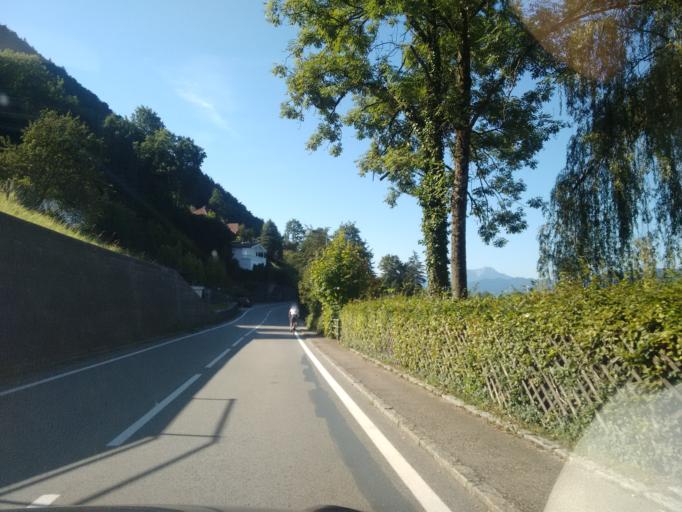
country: AT
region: Upper Austria
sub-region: Politischer Bezirk Vocklabruck
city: Attersee
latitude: 47.9146
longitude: 13.5772
